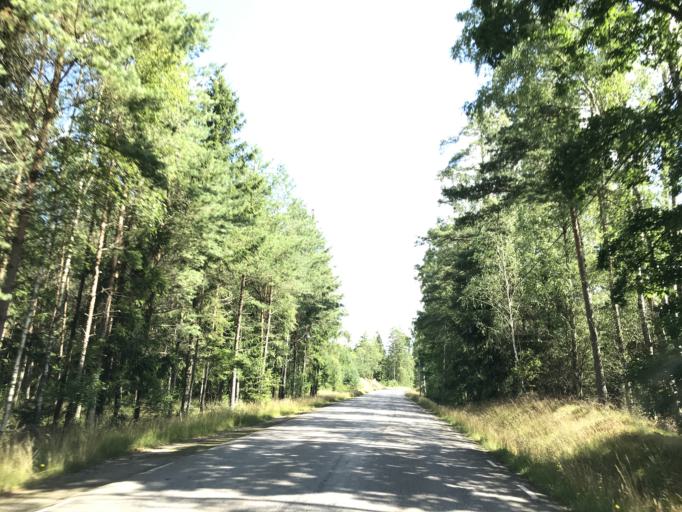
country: SE
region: Halland
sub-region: Laholms Kommun
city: Knared
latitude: 56.5197
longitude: 13.3579
